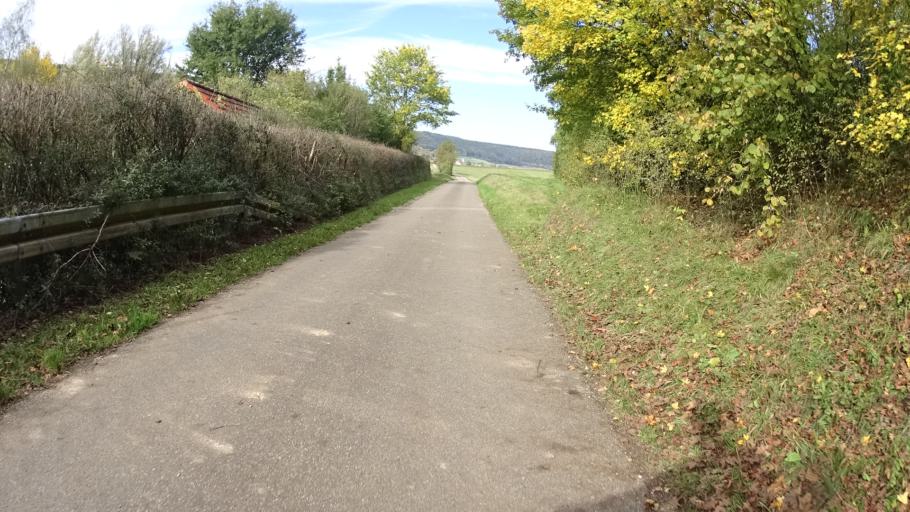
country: DE
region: Bavaria
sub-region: Upper Bavaria
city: Walting
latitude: 48.9151
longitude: 11.3061
